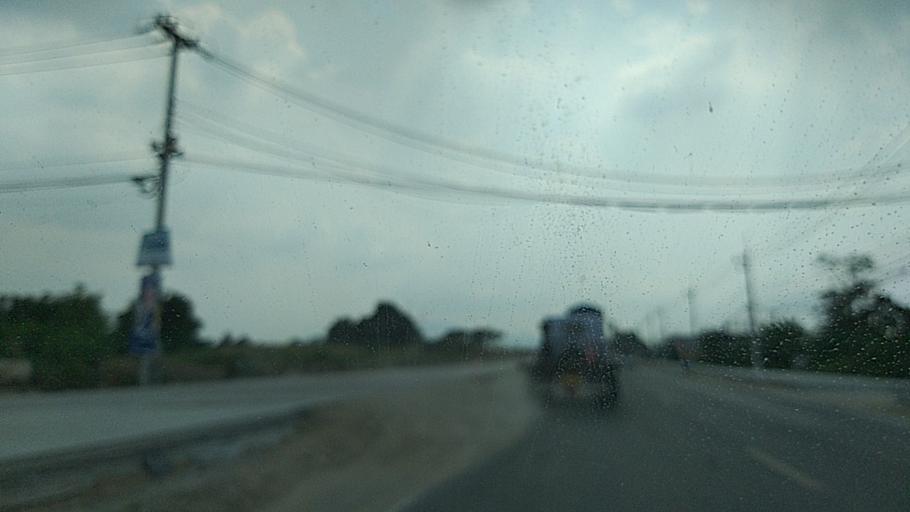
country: TH
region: Chon Buri
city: Ban Bueng
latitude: 13.3072
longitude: 101.1812
